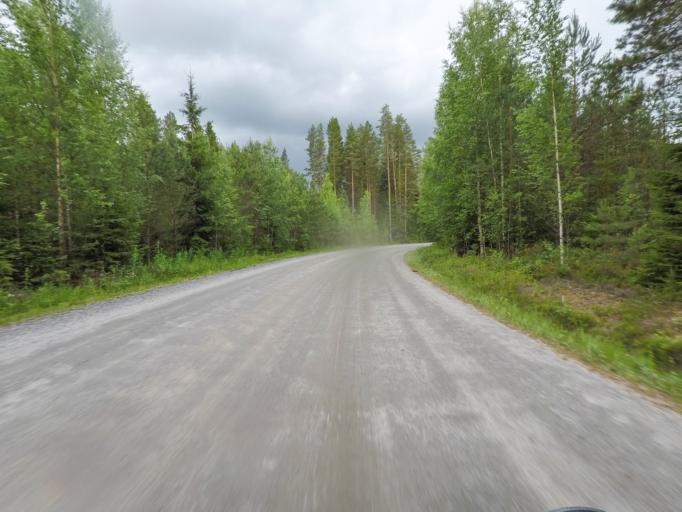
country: FI
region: Central Finland
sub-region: Jyvaeskylae
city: Hankasalmi
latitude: 62.4104
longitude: 26.6099
